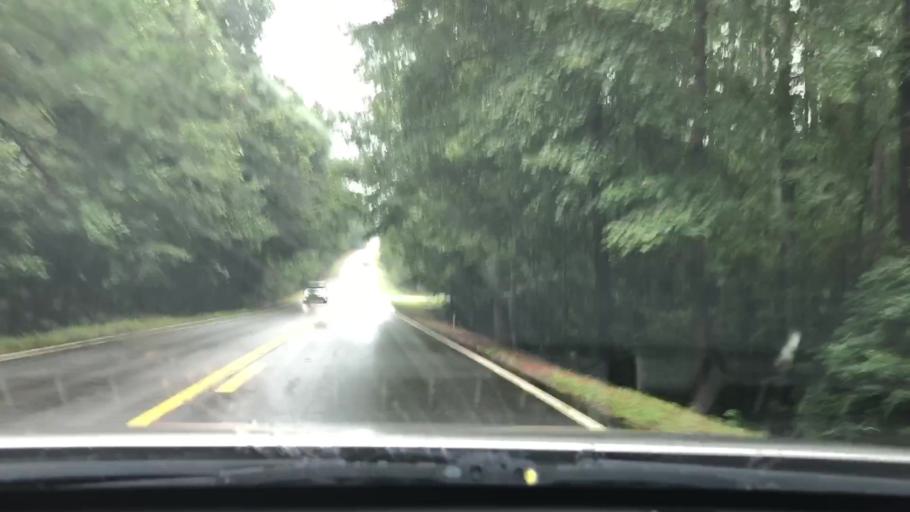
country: US
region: Georgia
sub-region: Lamar County
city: Barnesville
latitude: 33.0633
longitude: -84.2163
